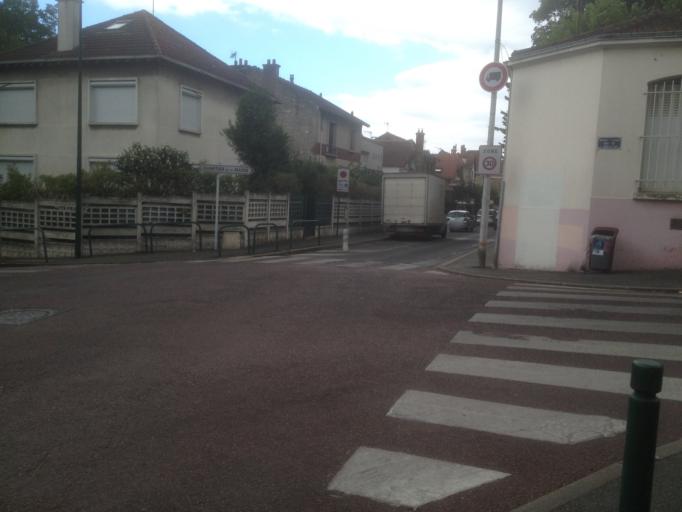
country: FR
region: Ile-de-France
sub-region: Departement du Val-de-Marne
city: Le Perreux-sur-Marne
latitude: 48.8439
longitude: 2.4918
